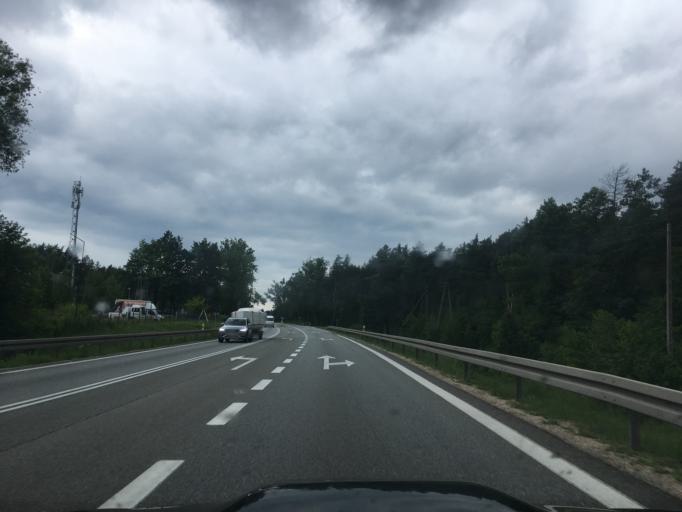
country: PL
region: Masovian Voivodeship
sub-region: Powiat otwocki
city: Celestynow
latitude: 52.0422
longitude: 21.3757
